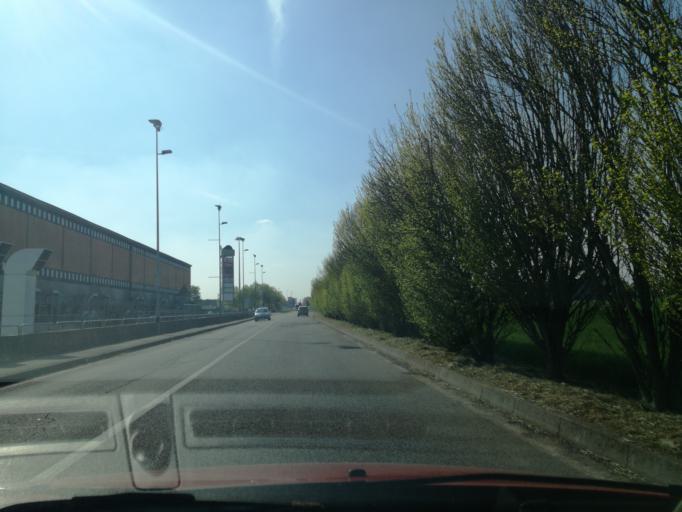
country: IT
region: Lombardy
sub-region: Provincia di Monza e Brianza
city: Cornate d'Adda
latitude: 45.6233
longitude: 9.4763
